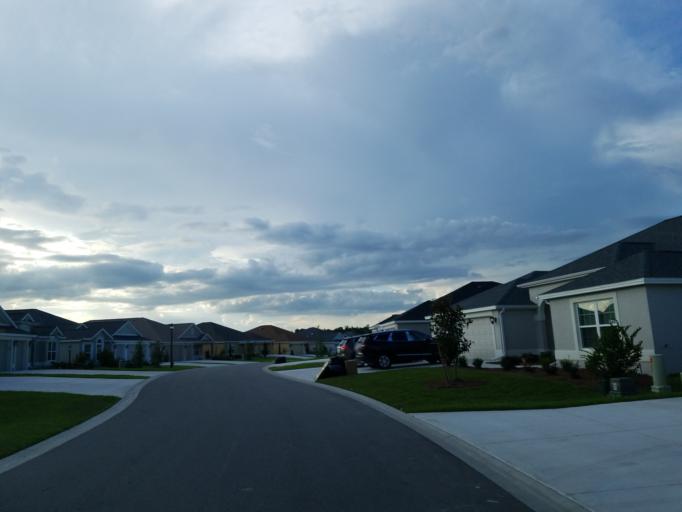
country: US
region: Florida
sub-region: Sumter County
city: Wildwood
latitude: 28.7959
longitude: -82.0240
